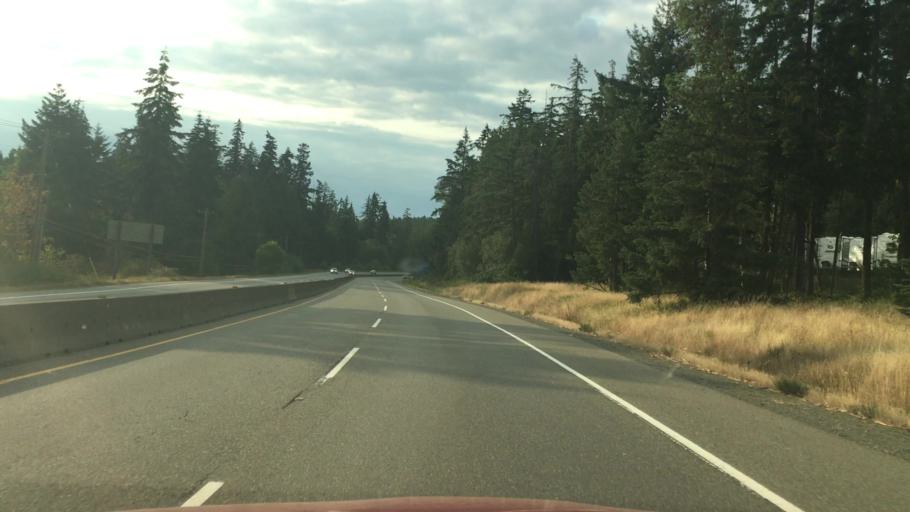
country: CA
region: British Columbia
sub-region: Regional District of Nanaimo
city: Parksville
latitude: 49.2877
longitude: -124.2512
